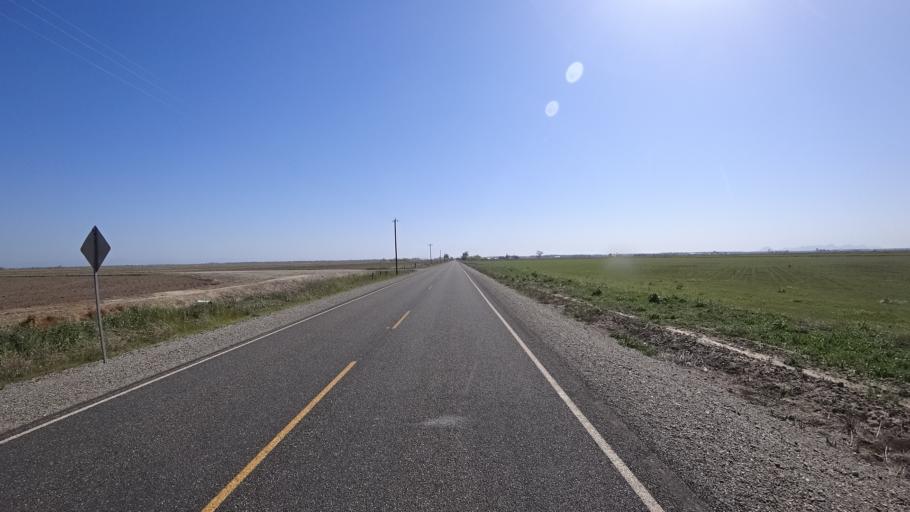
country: US
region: California
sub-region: Glenn County
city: Willows
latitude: 39.4578
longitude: -122.0621
